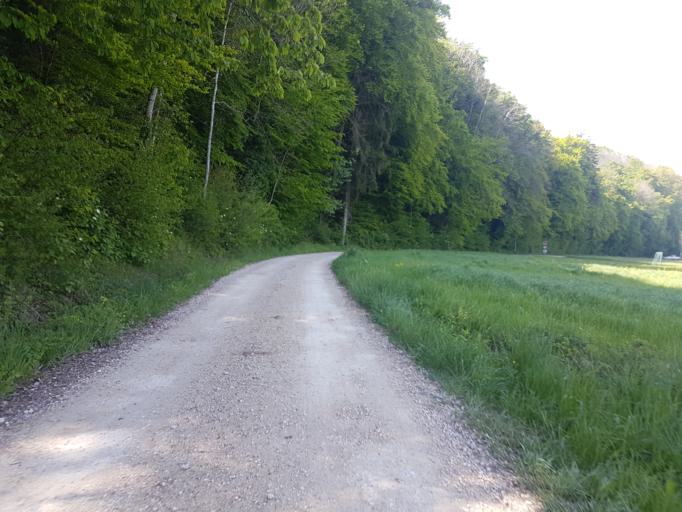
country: CH
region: Bern
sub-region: Seeland District
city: Tauffelen
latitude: 47.0486
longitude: 7.1626
